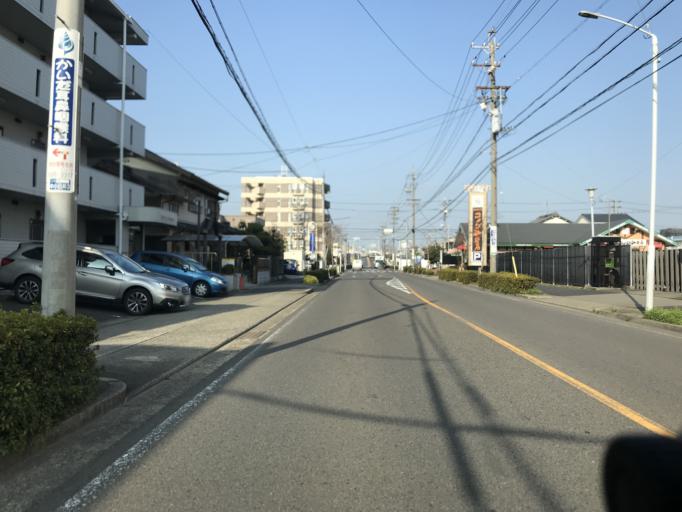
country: JP
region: Aichi
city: Nagoya-shi
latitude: 35.2136
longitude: 136.8692
